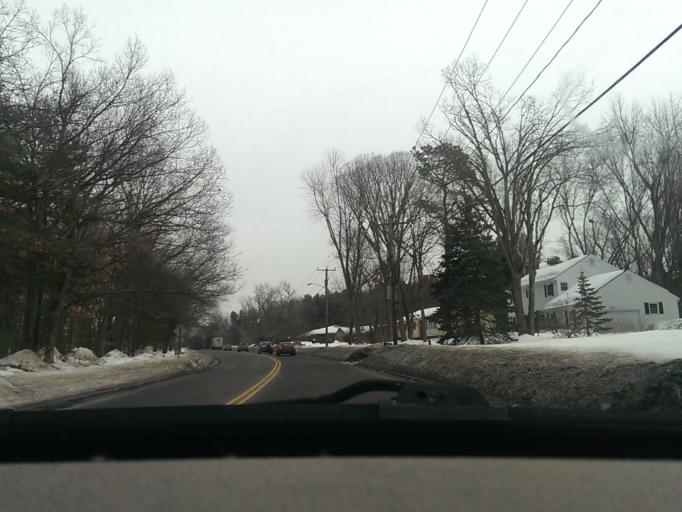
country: US
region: Massachusetts
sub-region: Hampden County
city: Longmeadow
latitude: 42.0622
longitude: -72.5506
